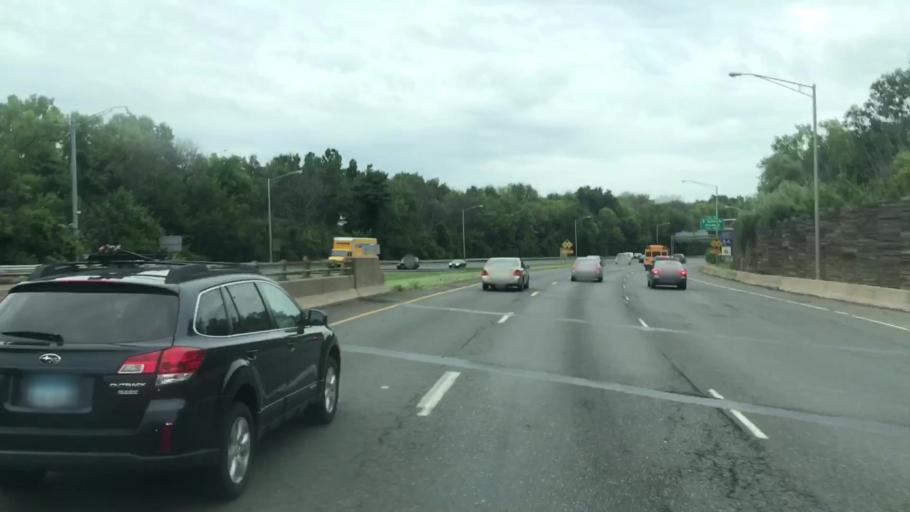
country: US
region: Connecticut
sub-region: Hartford County
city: West Hartford
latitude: 41.7320
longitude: -72.7553
